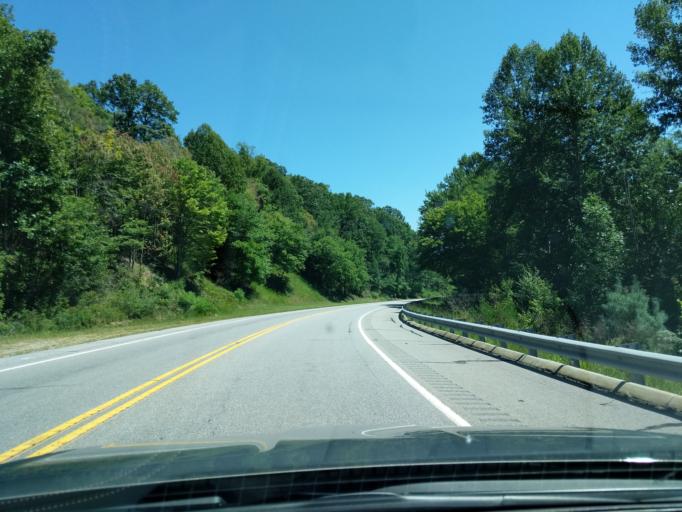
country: US
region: North Carolina
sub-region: Macon County
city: Franklin
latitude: 35.1357
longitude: -83.5125
